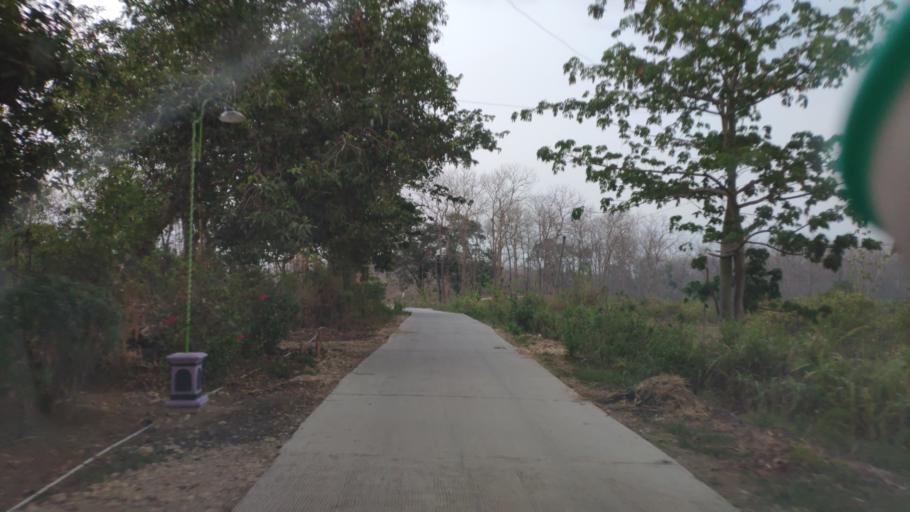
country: ID
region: Central Java
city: Kadengan
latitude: -7.1523
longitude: 111.3697
